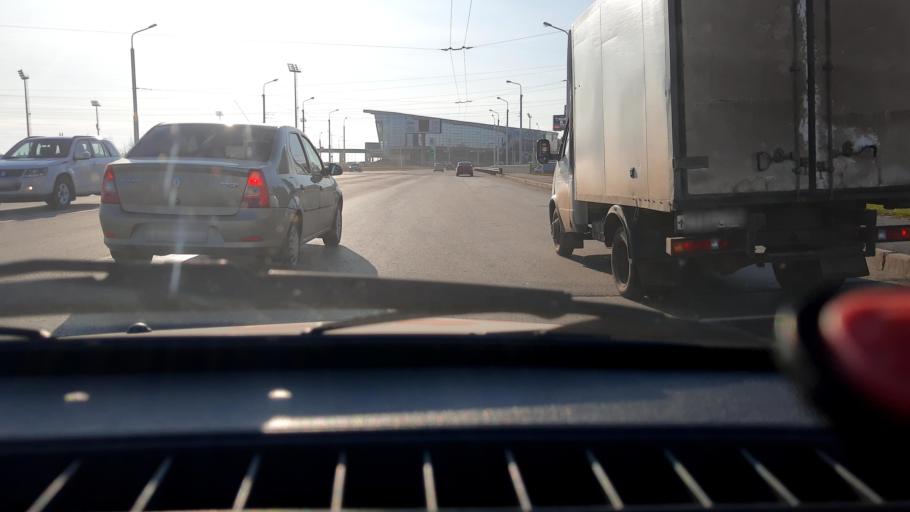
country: RU
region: Bashkortostan
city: Ufa
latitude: 54.7557
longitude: 56.0317
